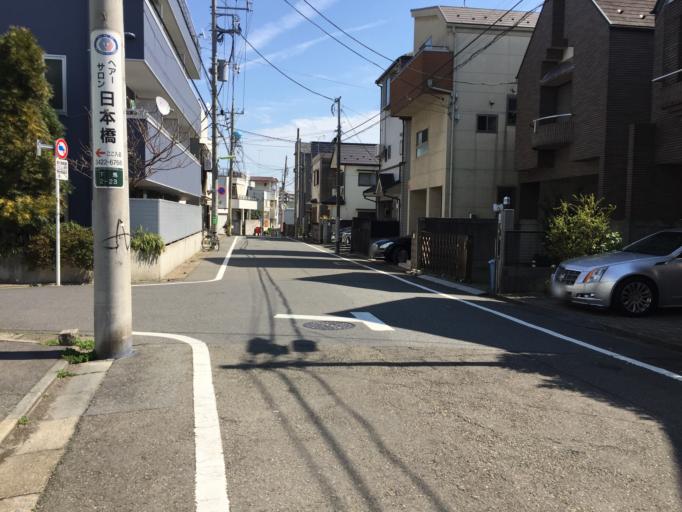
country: JP
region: Tokyo
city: Tokyo
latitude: 35.6406
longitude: 139.6779
